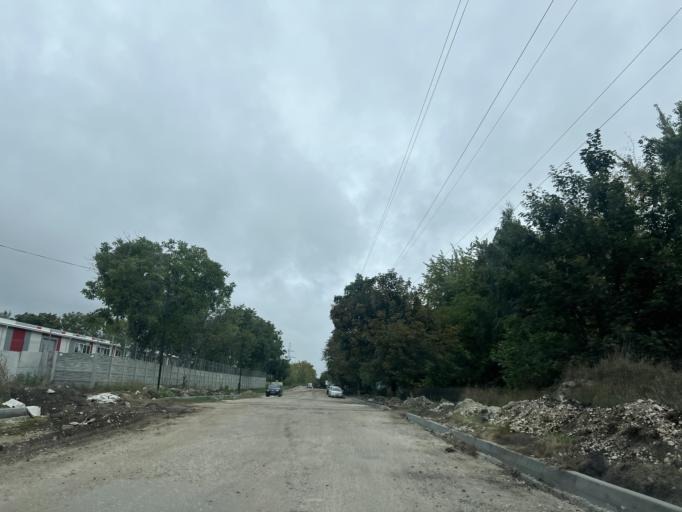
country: MD
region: Ungheni
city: Ungheni
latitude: 47.2242
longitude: 27.8070
